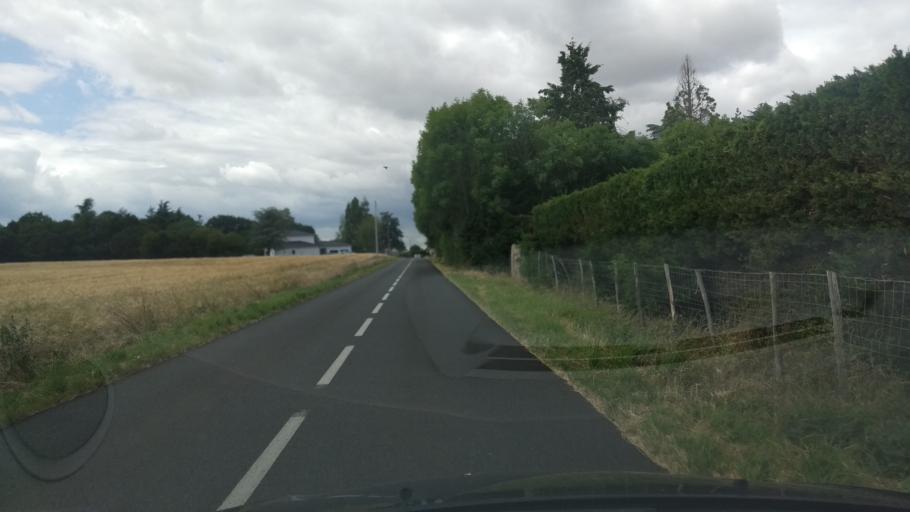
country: FR
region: Poitou-Charentes
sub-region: Departement de la Vienne
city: Vouille
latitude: 46.6277
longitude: 0.1934
